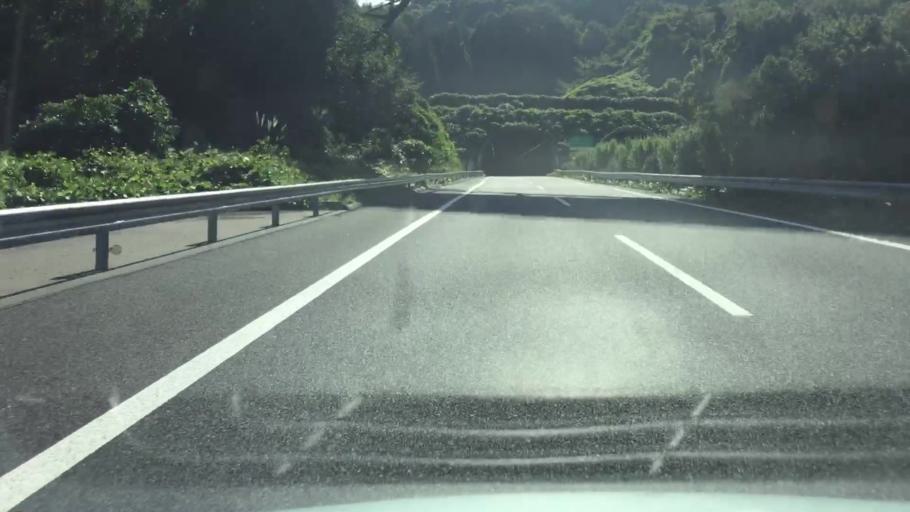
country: JP
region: Tochigi
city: Mooka
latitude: 36.3802
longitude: 140.0324
